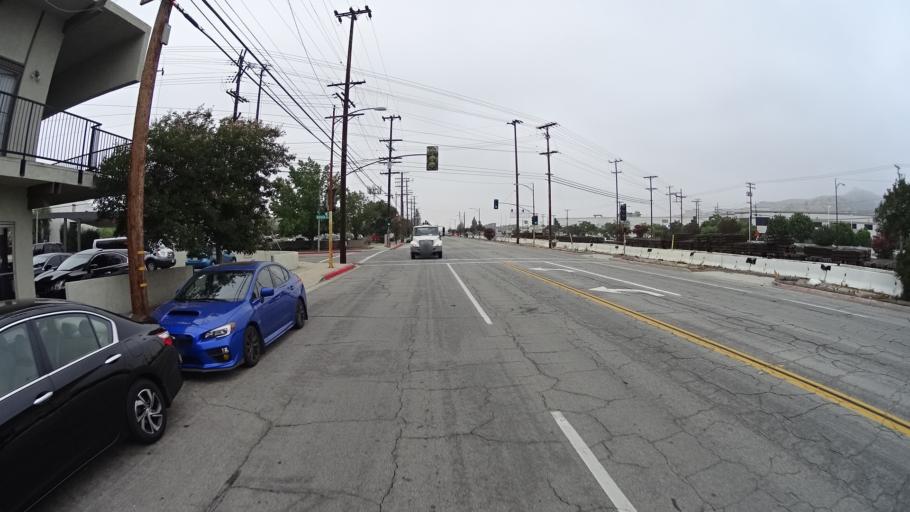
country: US
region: California
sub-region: Los Angeles County
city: Burbank
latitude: 34.2019
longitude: -118.3440
